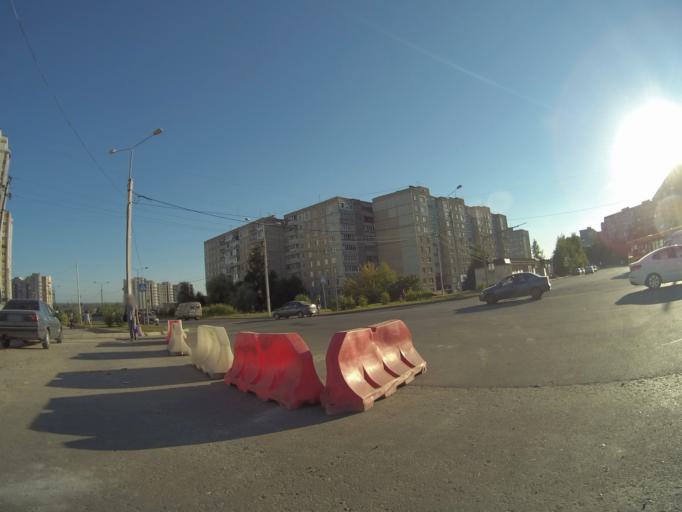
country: RU
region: Vladimir
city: Vladimir
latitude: 56.1072
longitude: 40.3564
